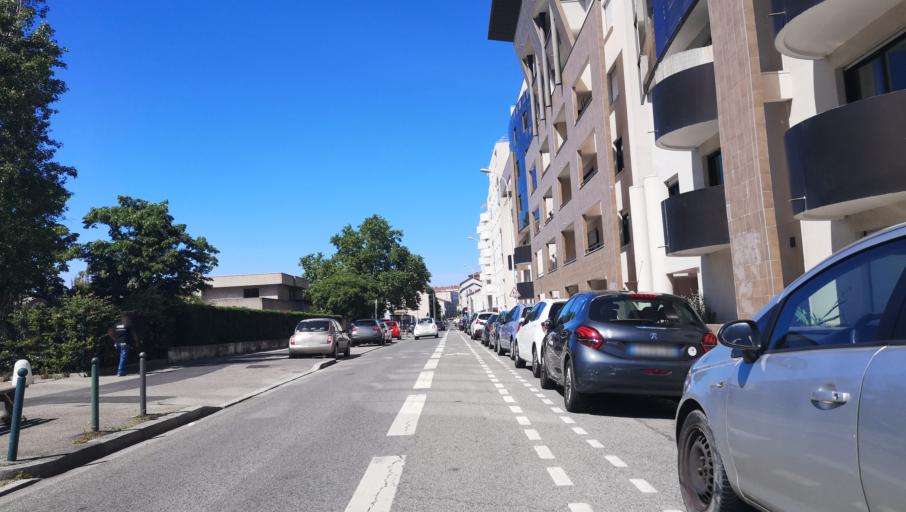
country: FR
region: Rhone-Alpes
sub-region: Departement du Rhone
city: Lyon
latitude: 45.7386
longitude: 4.8741
